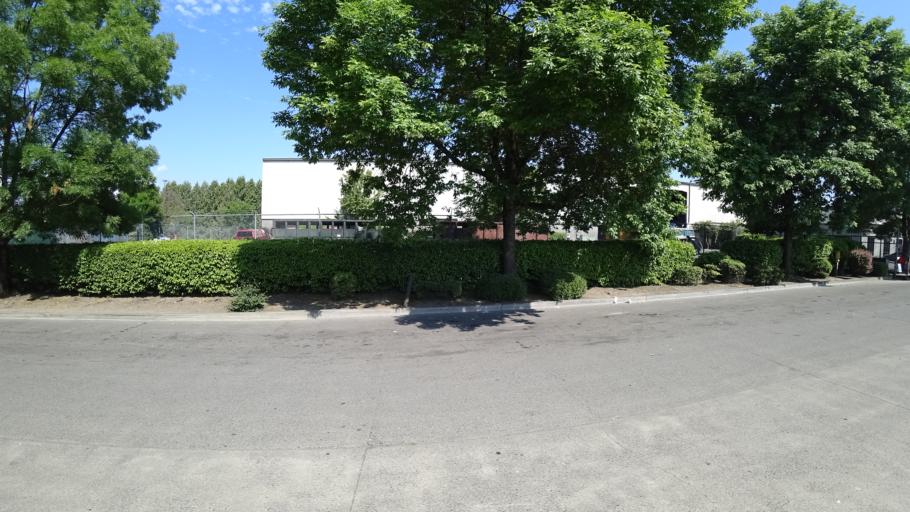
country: US
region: Oregon
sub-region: Multnomah County
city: Lents
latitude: 45.5583
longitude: -122.5321
